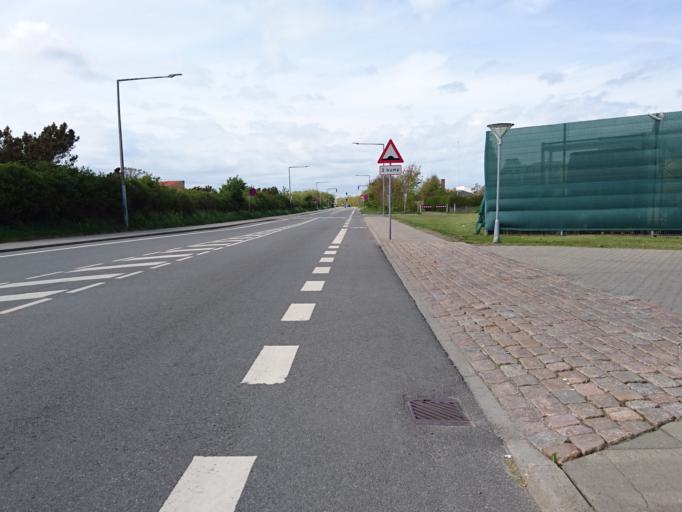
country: DK
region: North Denmark
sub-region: Frederikshavn Kommune
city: Skagen
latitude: 57.7261
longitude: 10.5624
